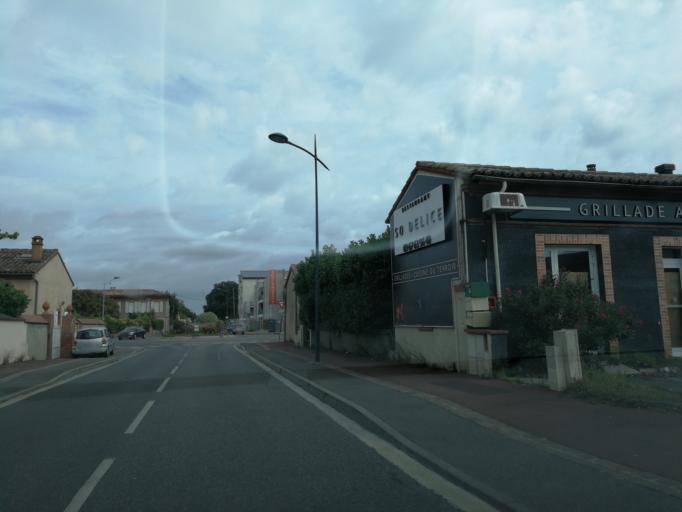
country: FR
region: Midi-Pyrenees
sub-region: Departement de la Haute-Garonne
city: Aucamville
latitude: 43.6555
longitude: 1.4322
